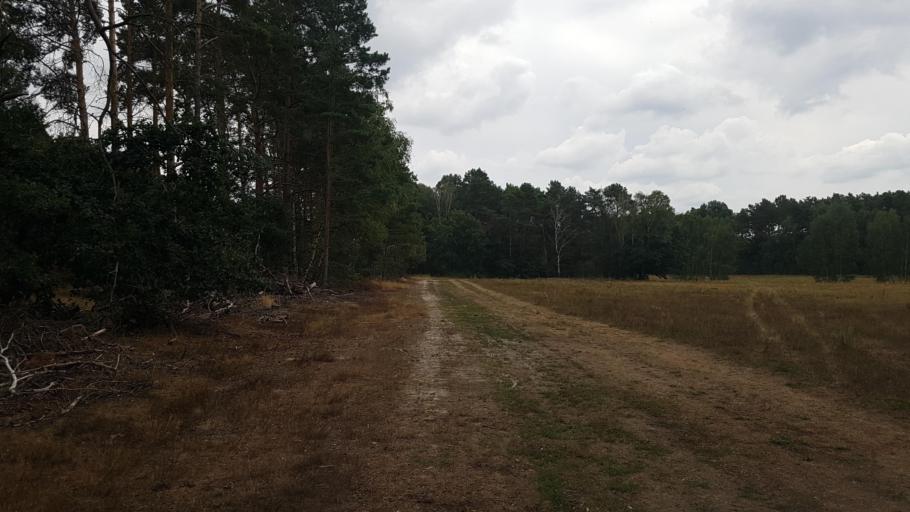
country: DE
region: Brandenburg
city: Sallgast
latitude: 51.6241
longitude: 13.8357
